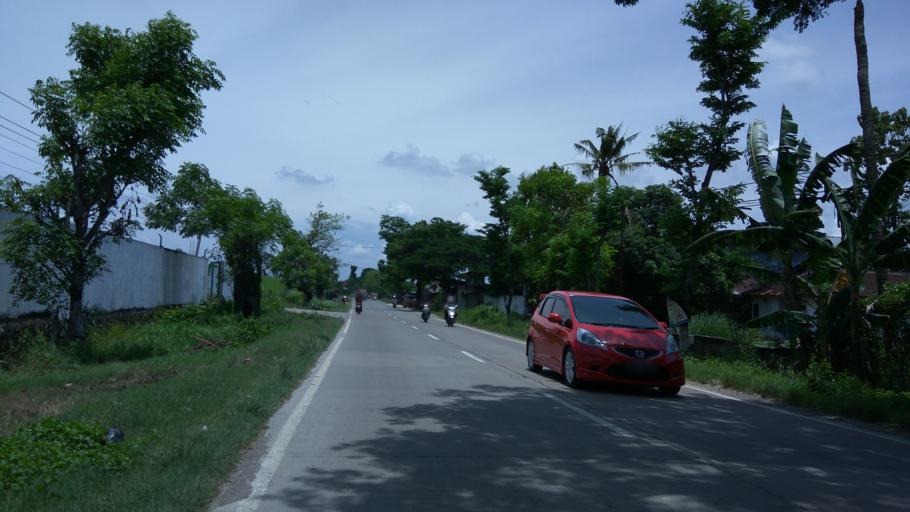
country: ID
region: Central Java
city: Mranggen
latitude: -7.0464
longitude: 110.5845
